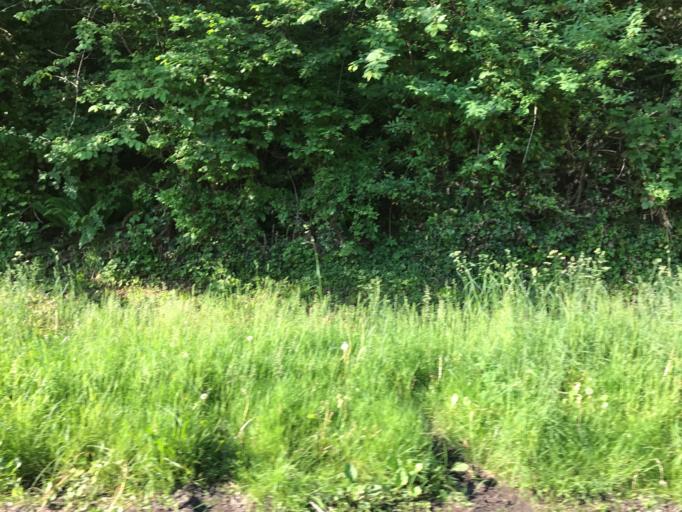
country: US
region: Washington
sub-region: King County
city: Seattle
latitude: 47.5845
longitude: -122.3105
